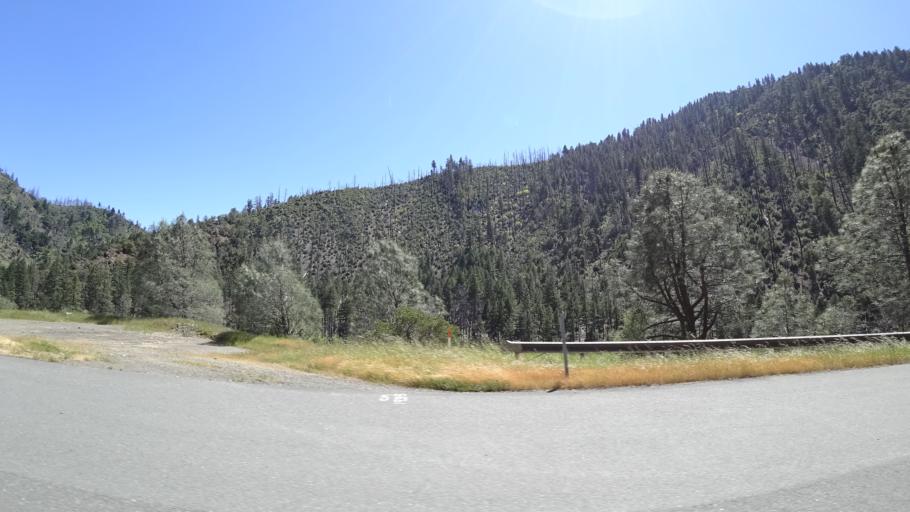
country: US
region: California
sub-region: Trinity County
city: Hayfork
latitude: 40.7928
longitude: -123.3586
